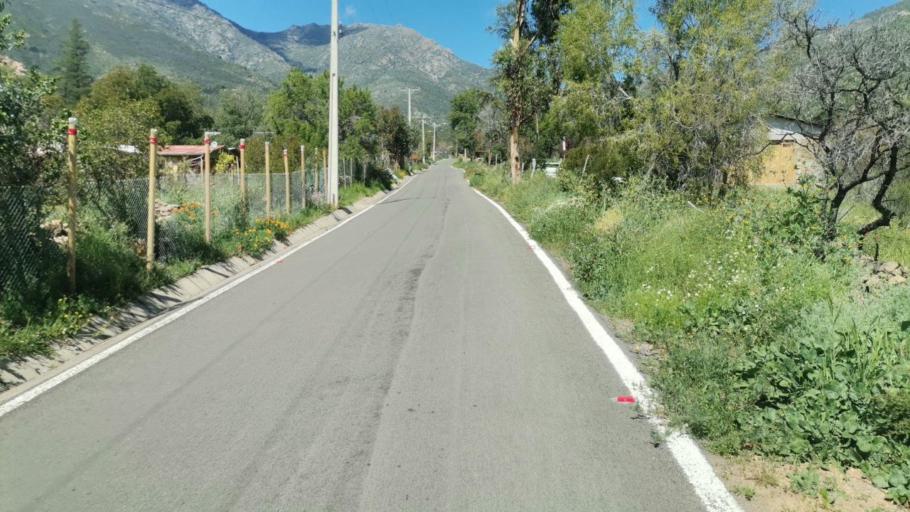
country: CL
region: Valparaiso
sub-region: Provincia de Marga Marga
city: Limache
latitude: -33.1906
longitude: -71.0983
